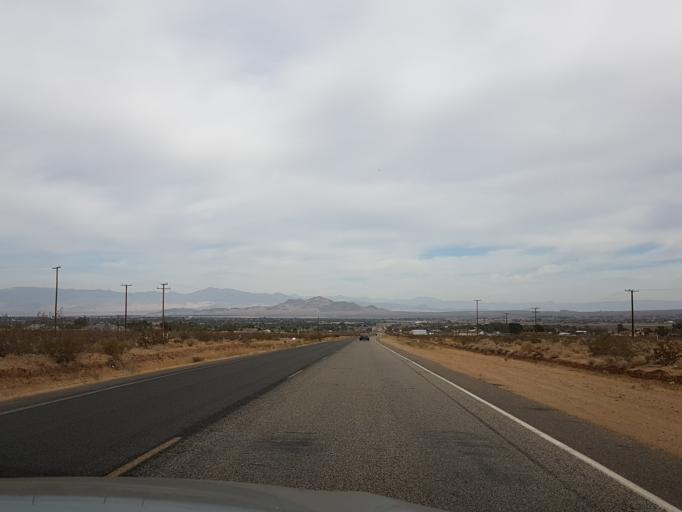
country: US
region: California
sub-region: Kern County
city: Ridgecrest
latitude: 35.5851
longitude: -117.7040
